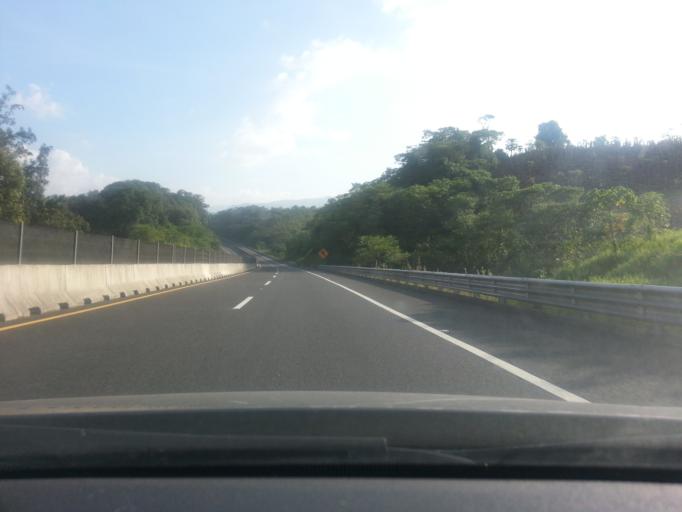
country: MX
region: Puebla
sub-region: Xicotepec
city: San Lorenzo
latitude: 20.4058
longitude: -97.9404
